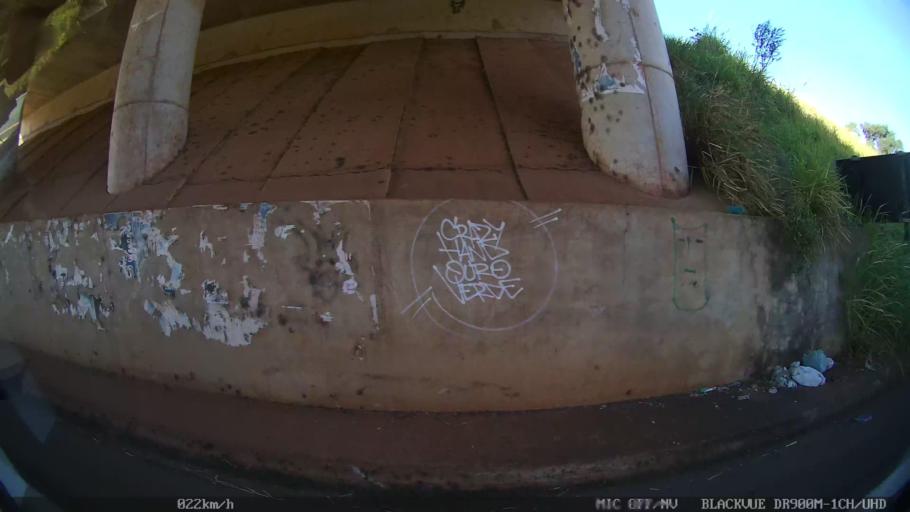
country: BR
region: Sao Paulo
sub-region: Batatais
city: Batatais
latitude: -20.9160
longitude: -47.5838
